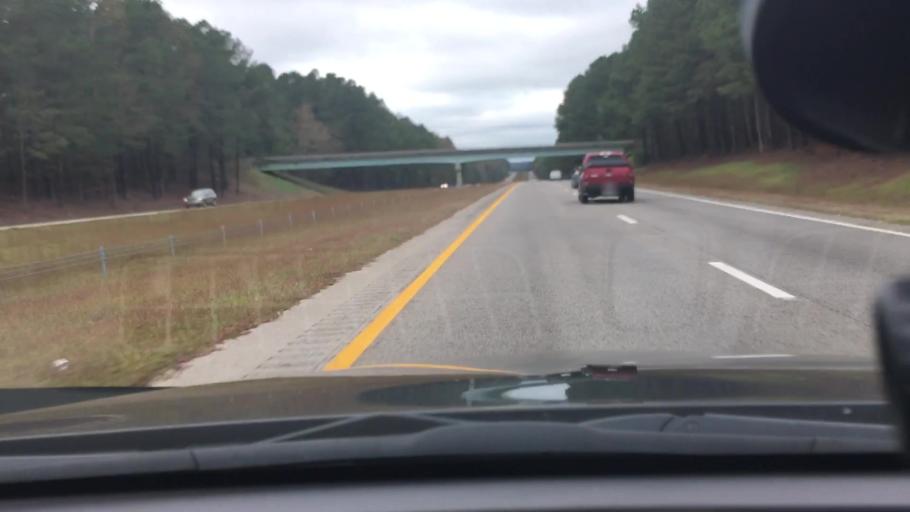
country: US
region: North Carolina
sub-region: Wake County
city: Zebulon
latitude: 35.8097
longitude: -78.2217
